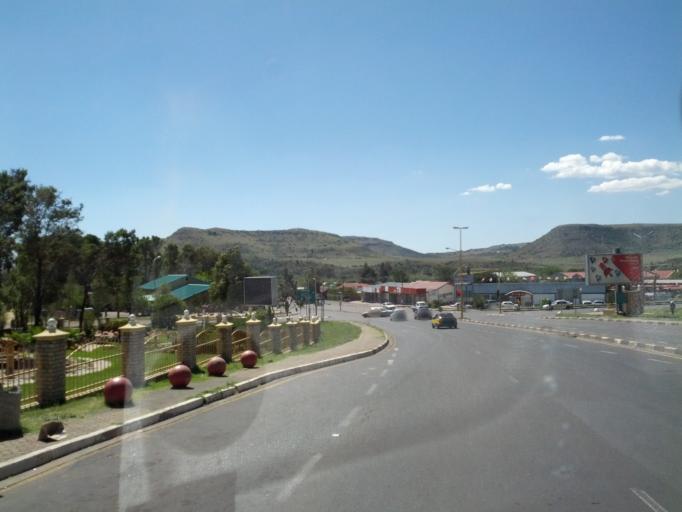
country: LS
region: Maseru
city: Maseru
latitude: -29.3051
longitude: 27.4675
